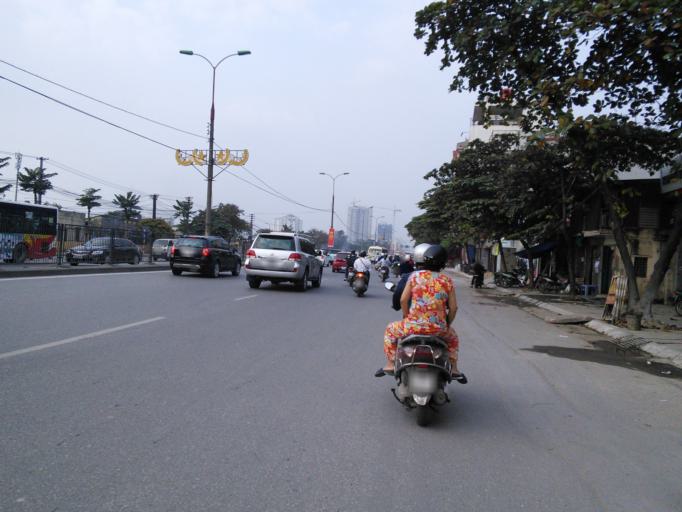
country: VN
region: Ha Noi
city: Van Dien
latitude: 20.9744
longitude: 105.8410
